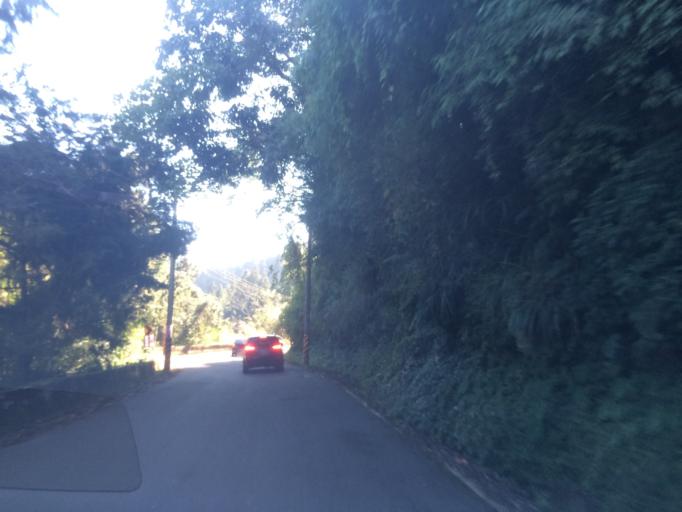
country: TW
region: Taiwan
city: Lugu
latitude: 23.6575
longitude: 120.7792
